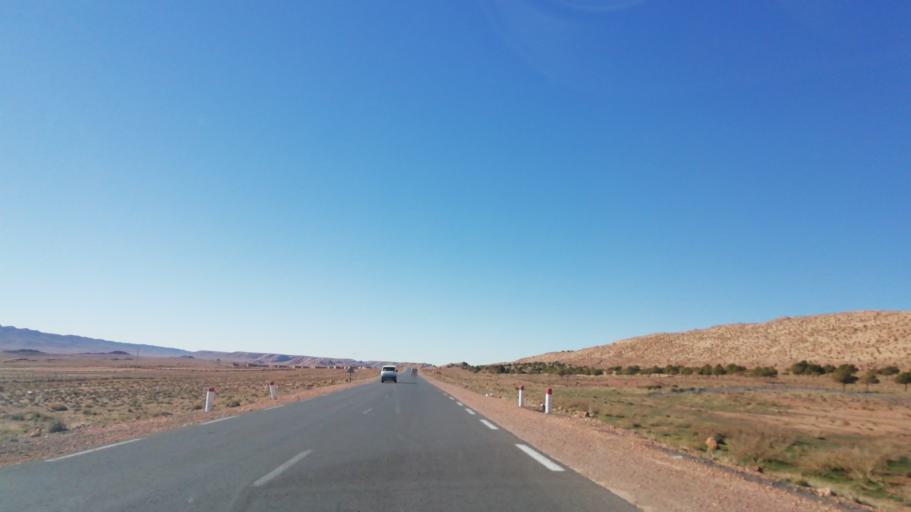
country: DZ
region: El Bayadh
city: El Bayadh
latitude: 33.6167
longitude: 1.1848
